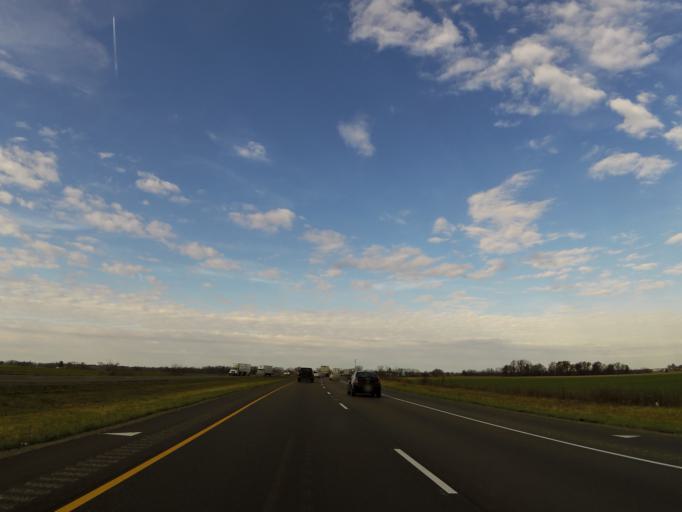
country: US
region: Illinois
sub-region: Washington County
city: Okawville
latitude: 38.4317
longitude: -89.5110
